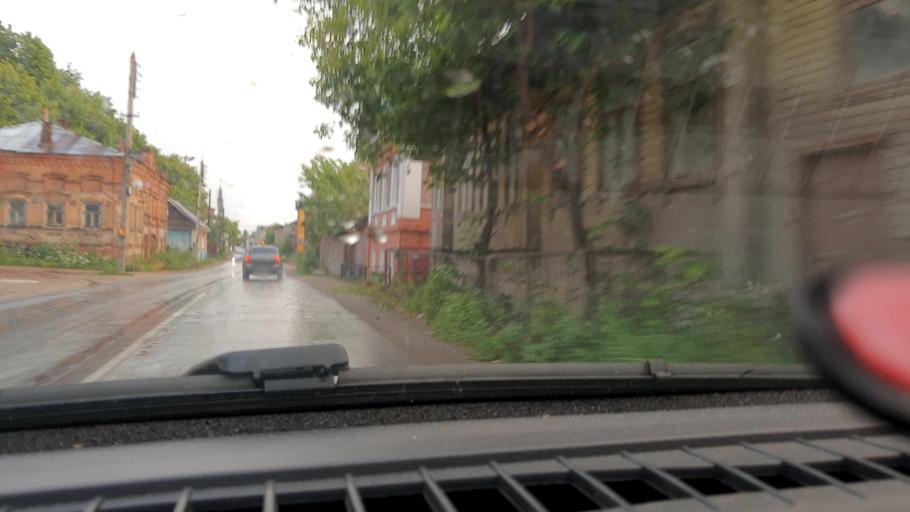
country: RU
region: Nizjnij Novgorod
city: Gorodets
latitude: 56.6481
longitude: 43.4649
